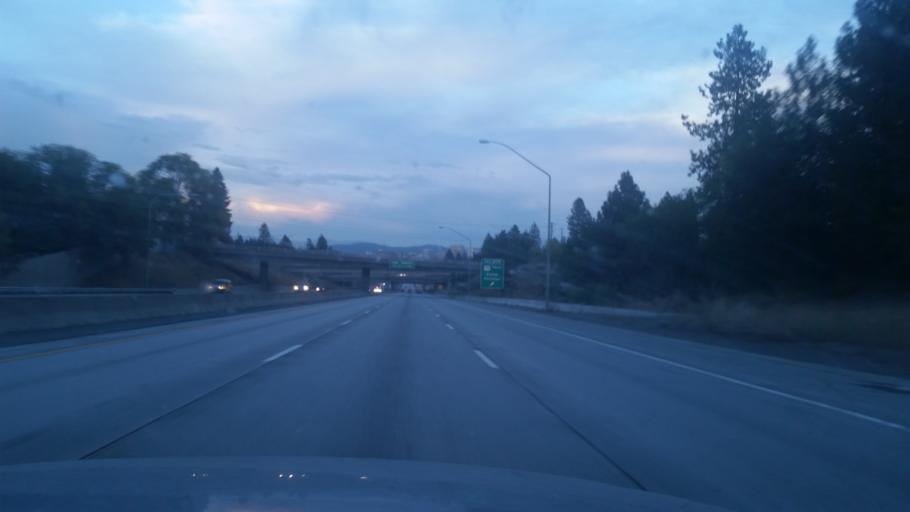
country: US
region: Washington
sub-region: Spokane County
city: Spokane
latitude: 47.6441
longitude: -117.4571
